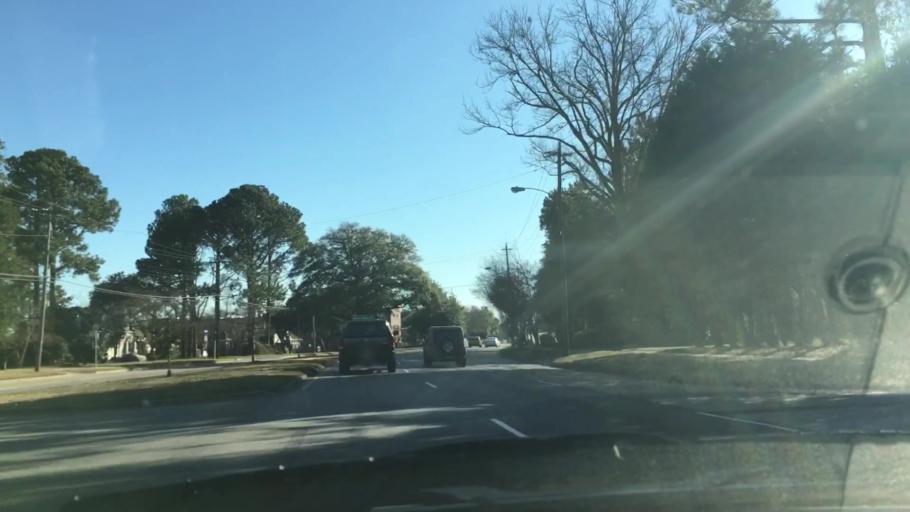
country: US
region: Virginia
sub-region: City of Norfolk
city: Norfolk
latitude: 36.8928
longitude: -76.2790
